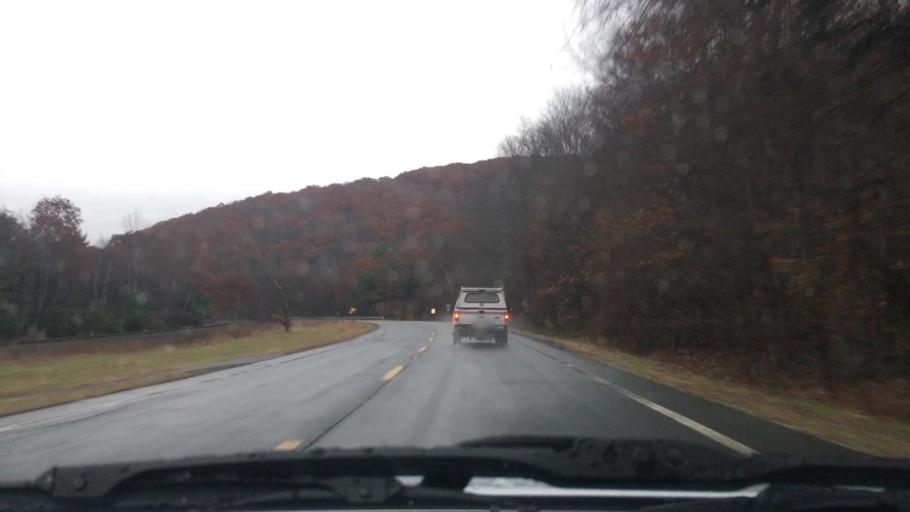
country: US
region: Massachusetts
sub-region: Hampshire County
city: Westhampton
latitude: 42.2361
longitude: -72.8981
